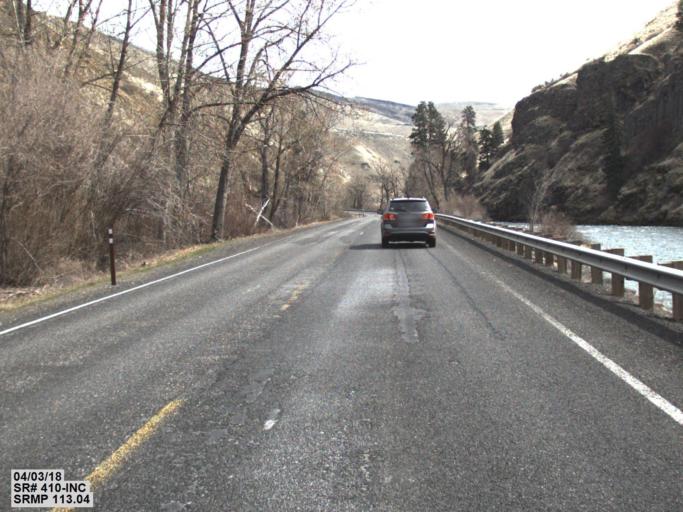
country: US
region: Washington
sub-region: Yakima County
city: Tieton
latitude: 46.7695
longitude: -120.8421
